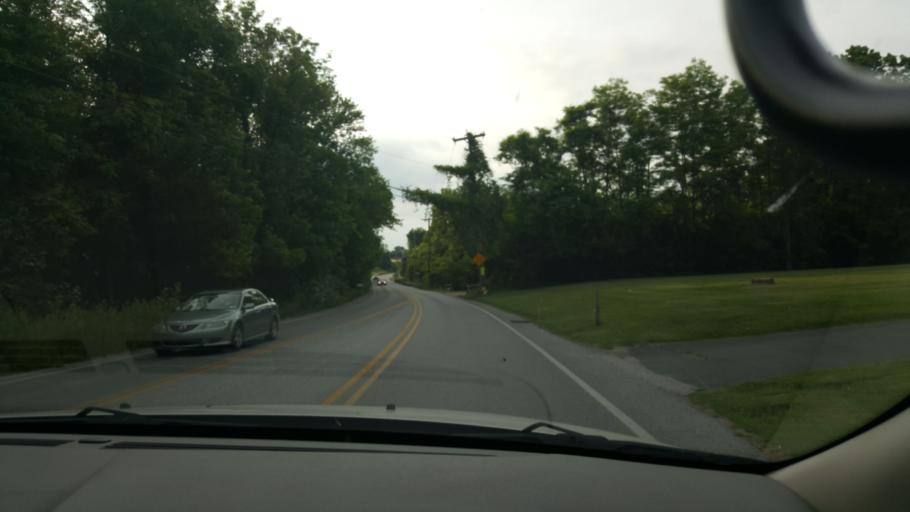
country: US
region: Pennsylvania
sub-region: York County
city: Shiloh
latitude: 39.9995
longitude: -76.7975
